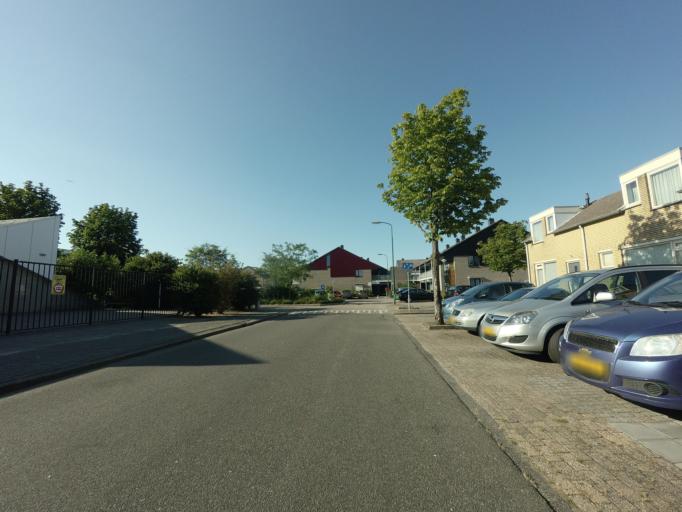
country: NL
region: Utrecht
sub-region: Stichtse Vecht
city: Spechtenkamp
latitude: 52.1367
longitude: 5.0203
